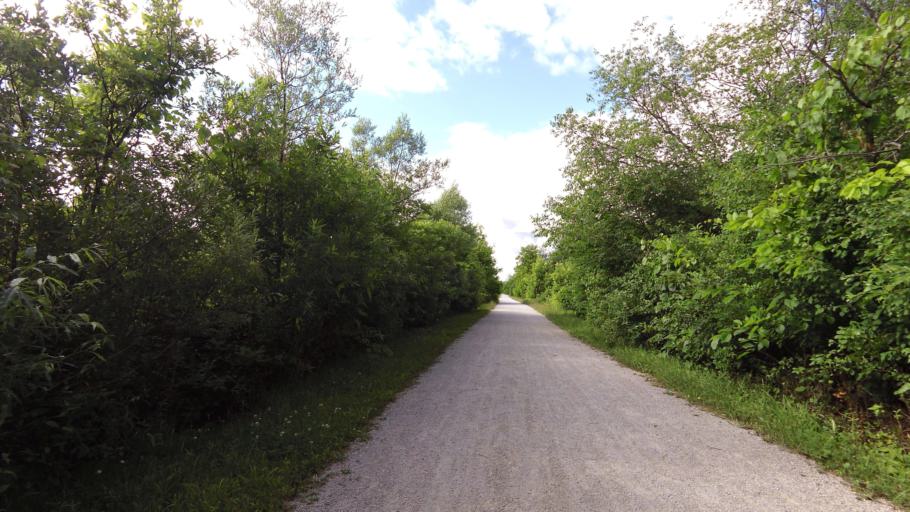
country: CA
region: Ontario
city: Orangeville
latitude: 43.8020
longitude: -79.9320
